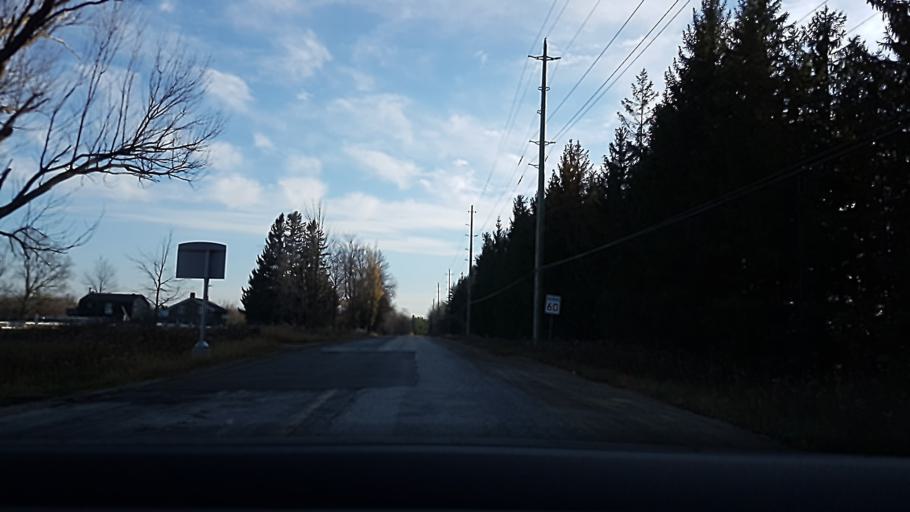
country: CA
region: Ontario
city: Barrie
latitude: 44.3774
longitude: -79.5535
